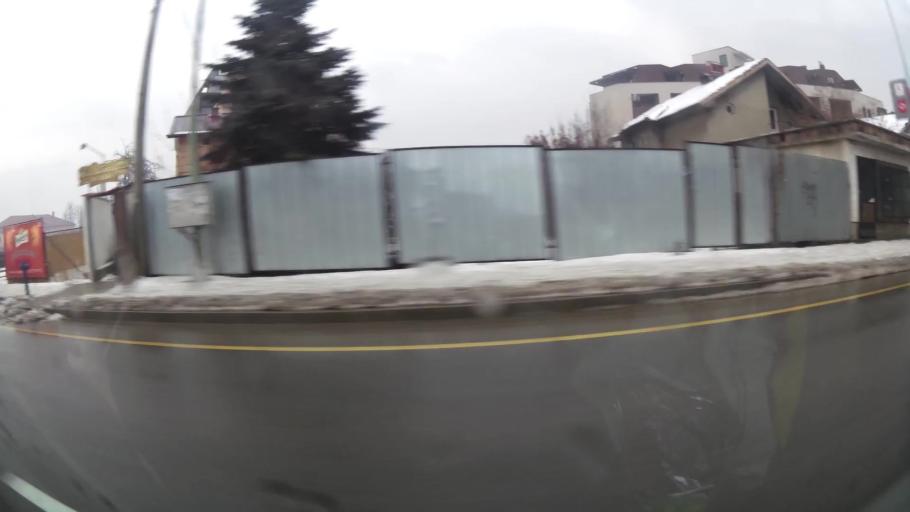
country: BG
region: Sofia-Capital
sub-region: Stolichna Obshtina
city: Sofia
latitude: 42.6788
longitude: 23.2542
